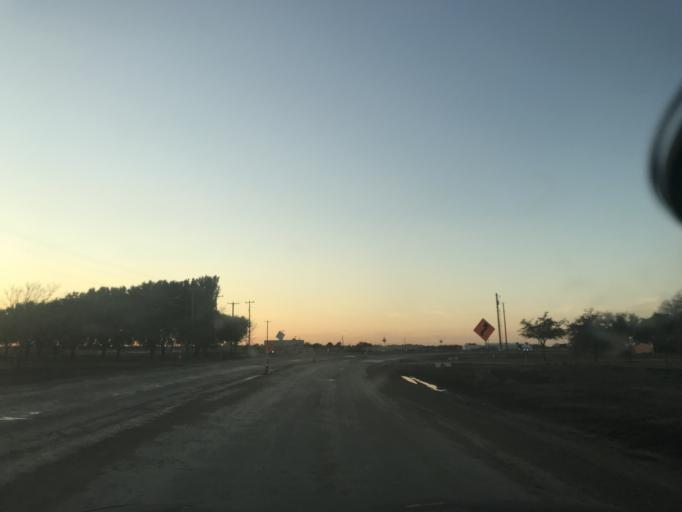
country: US
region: Texas
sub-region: Williamson County
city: Hutto
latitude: 30.5134
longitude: -97.5326
